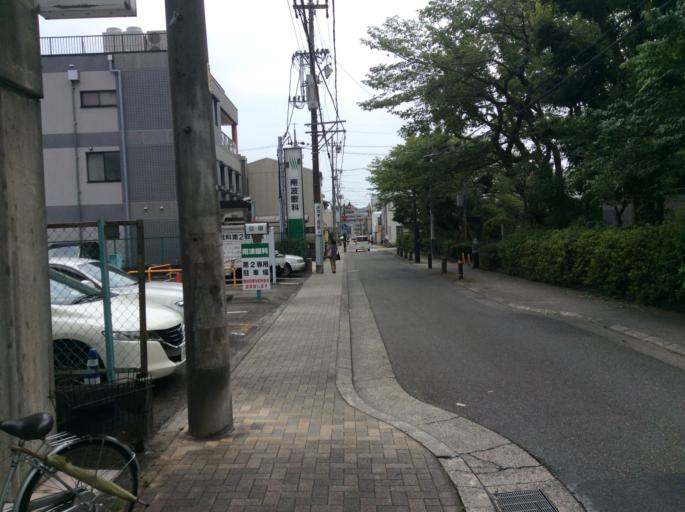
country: JP
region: Shizuoka
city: Shizuoka-shi
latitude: 34.9807
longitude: 138.3909
